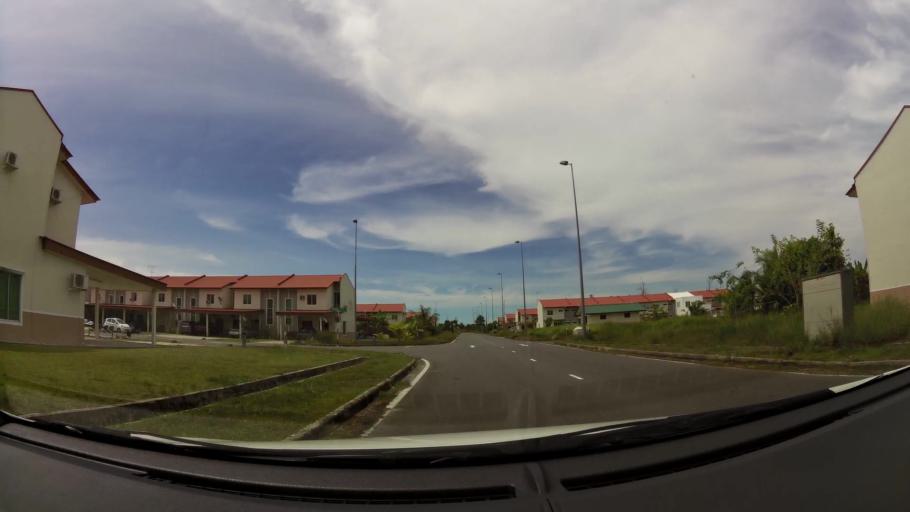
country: BN
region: Belait
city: Kuala Belait
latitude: 4.5901
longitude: 114.2698
